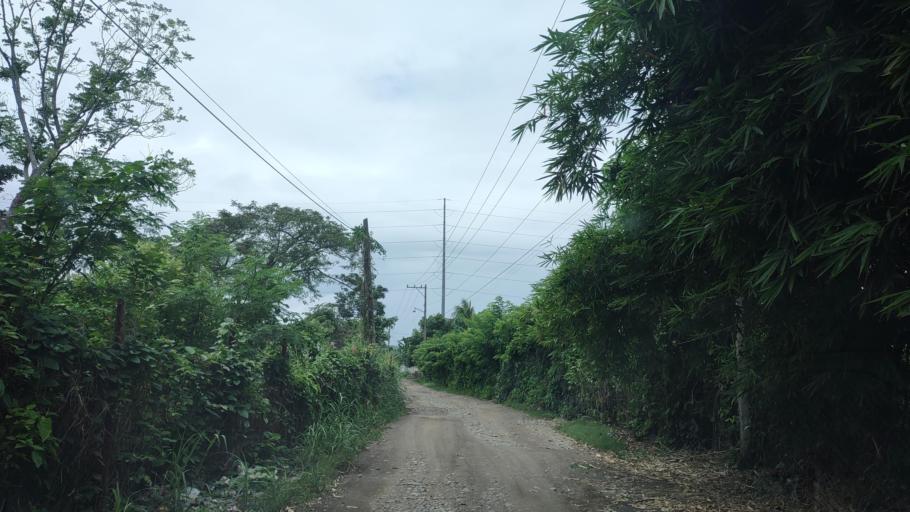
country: MX
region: Veracruz
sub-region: Papantla
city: Residencial Tajin
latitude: 20.5920
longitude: -97.4210
